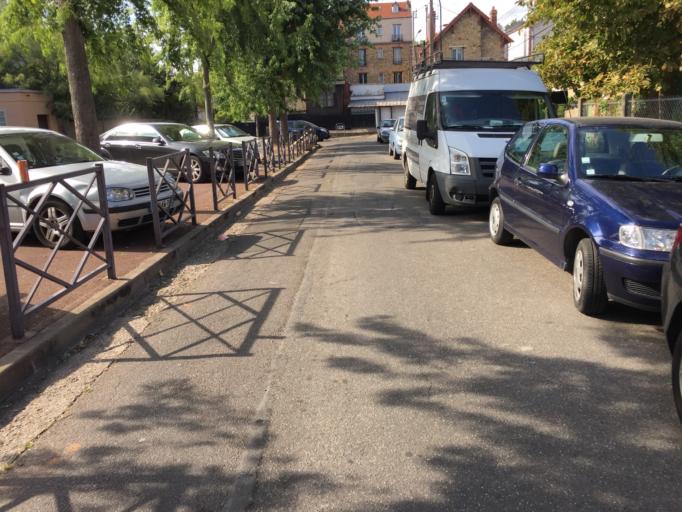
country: FR
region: Ile-de-France
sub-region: Departement du Val-d'Oise
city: Argenteuil
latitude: 48.9517
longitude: 2.2680
